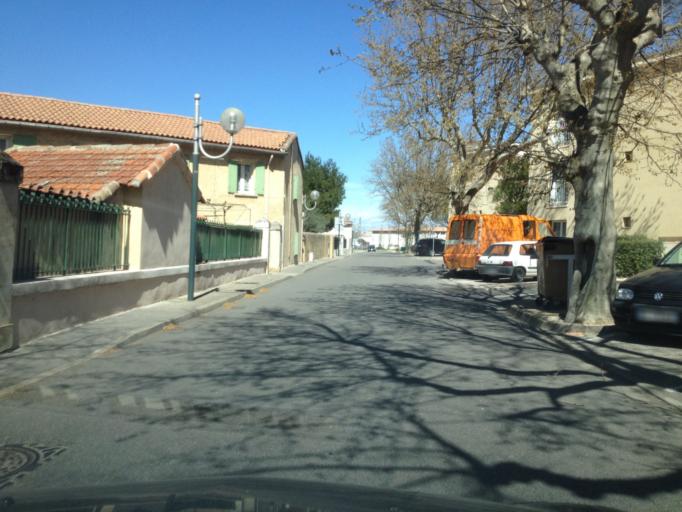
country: FR
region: Provence-Alpes-Cote d'Azur
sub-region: Departement du Vaucluse
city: Le Pontet
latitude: 43.9653
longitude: 4.8602
